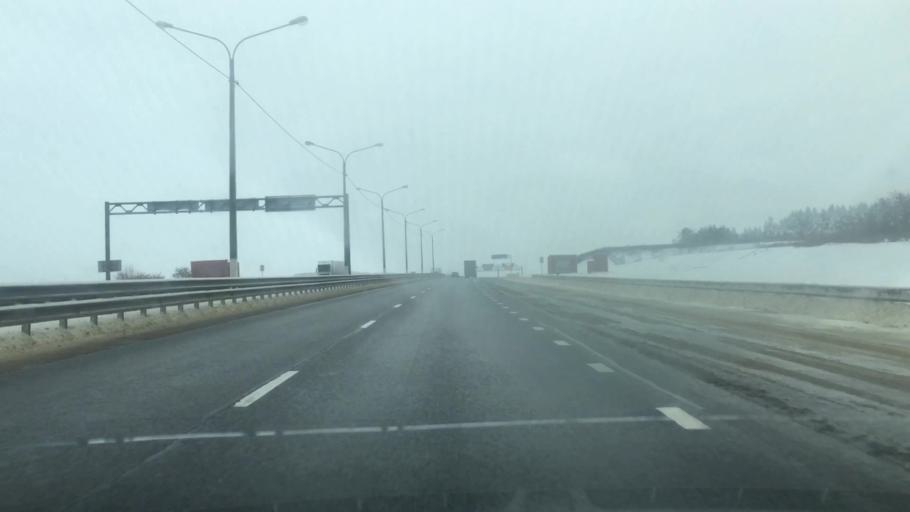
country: RU
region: Tula
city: Yefremov
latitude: 53.1594
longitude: 38.2496
